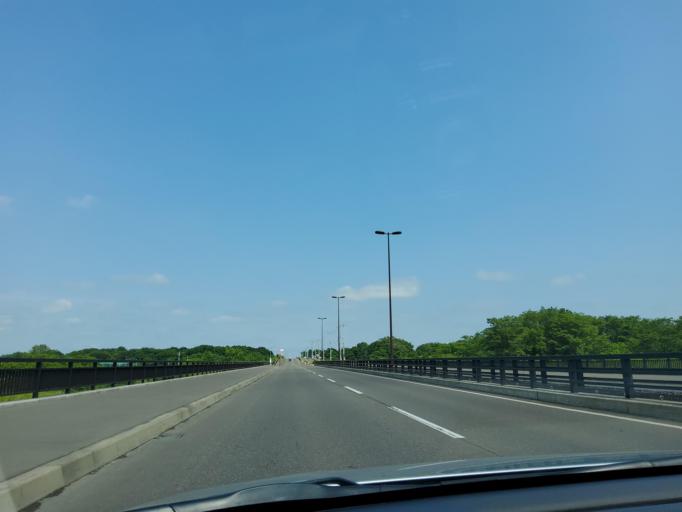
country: JP
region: Hokkaido
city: Obihiro
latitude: 42.9121
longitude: 143.0621
